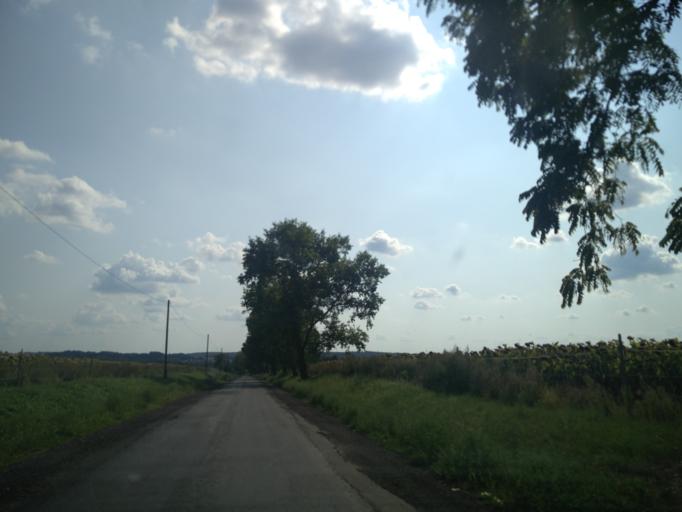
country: HU
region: Zala
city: Zalaegerszeg
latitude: 46.8894
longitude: 16.7573
